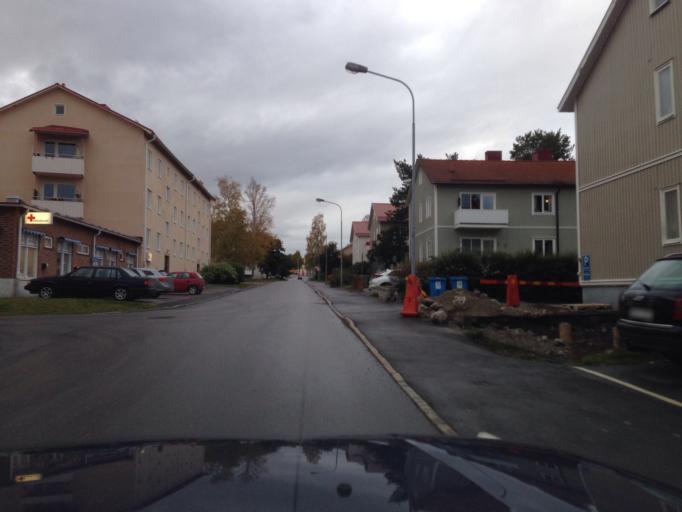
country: SE
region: Vaesternorrland
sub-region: Sundsvalls Kommun
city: Sundsvall
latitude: 62.3981
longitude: 17.3302
